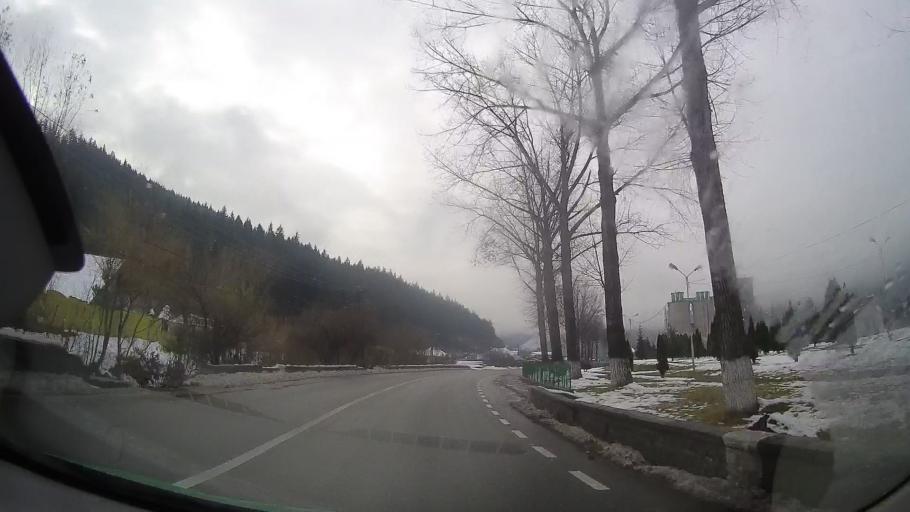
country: RO
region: Neamt
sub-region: Comuna Tasca
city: Tasca
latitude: 46.8958
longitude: 26.0389
